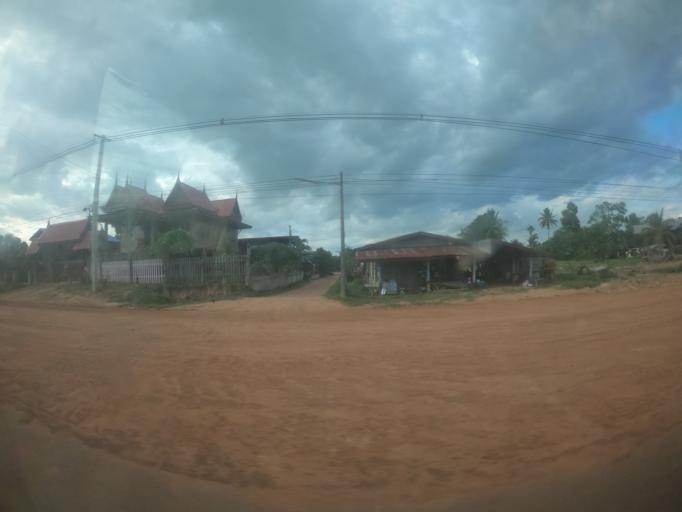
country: TH
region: Surin
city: Kap Choeng
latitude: 14.4604
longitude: 103.6601
